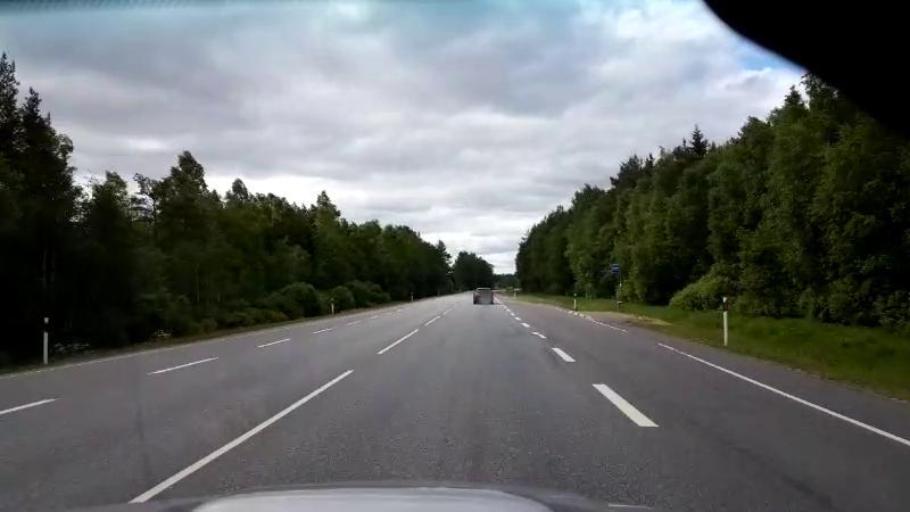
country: EE
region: Raplamaa
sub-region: Maerjamaa vald
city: Marjamaa
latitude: 58.9461
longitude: 24.4676
